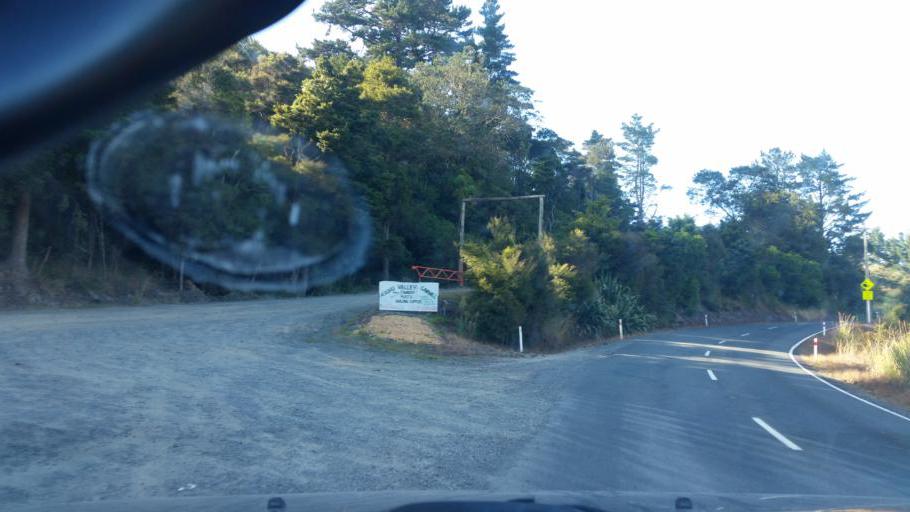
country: NZ
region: Northland
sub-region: Kaipara District
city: Dargaville
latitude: -35.8118
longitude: 173.7275
